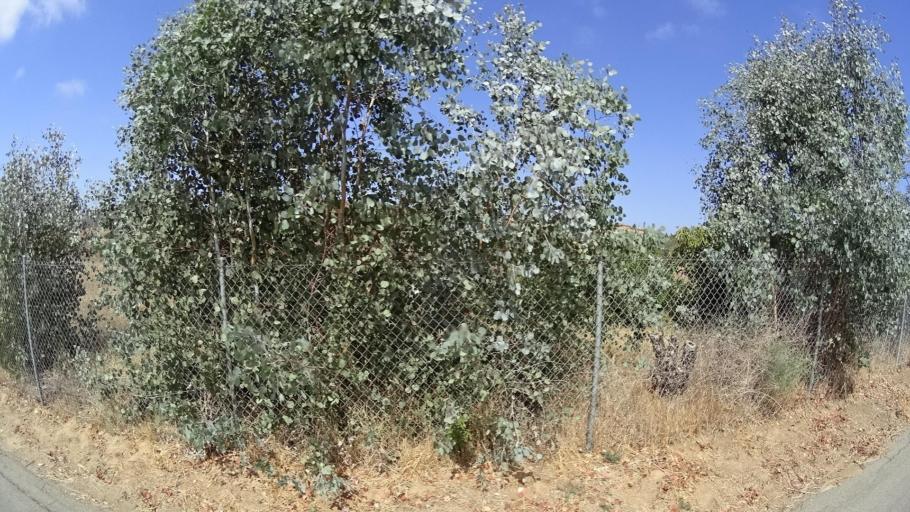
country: US
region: California
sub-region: San Diego County
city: Fallbrook
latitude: 33.4211
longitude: -117.2323
